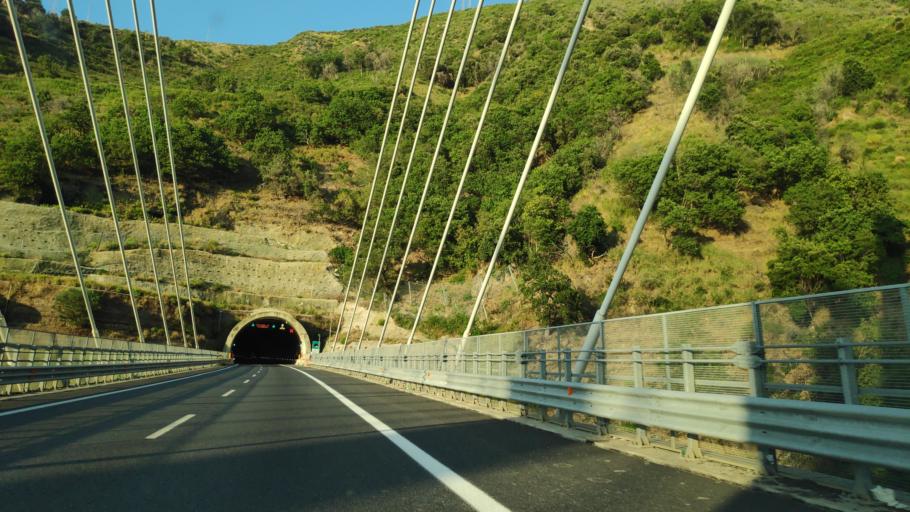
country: IT
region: Calabria
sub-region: Provincia di Reggio Calabria
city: Bagnara Calabra
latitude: 38.2551
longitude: 15.7692
